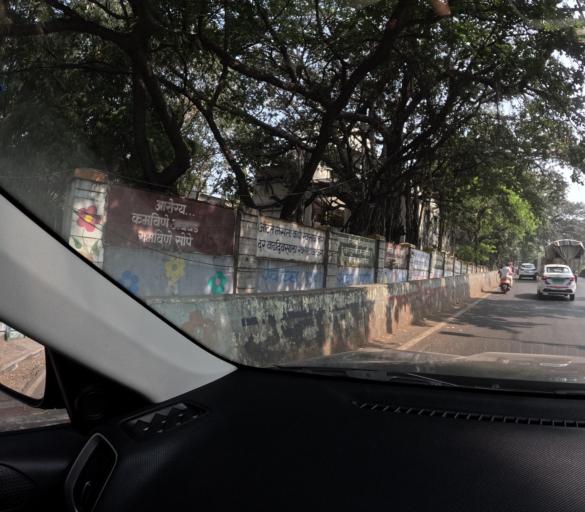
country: IN
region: Maharashtra
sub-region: Pune Division
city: Pune
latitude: 18.5247
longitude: 73.8693
